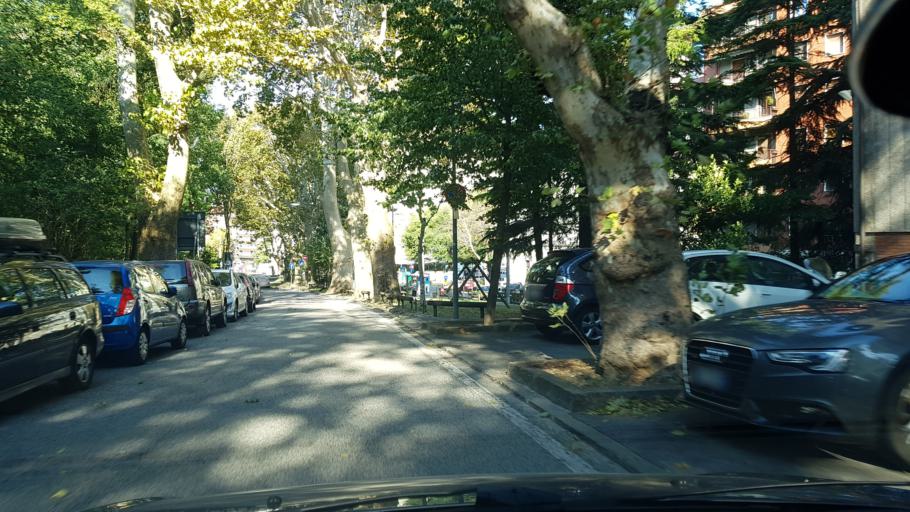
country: IT
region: Friuli Venezia Giulia
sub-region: Provincia di Trieste
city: Trieste
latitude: 45.6540
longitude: 13.8002
